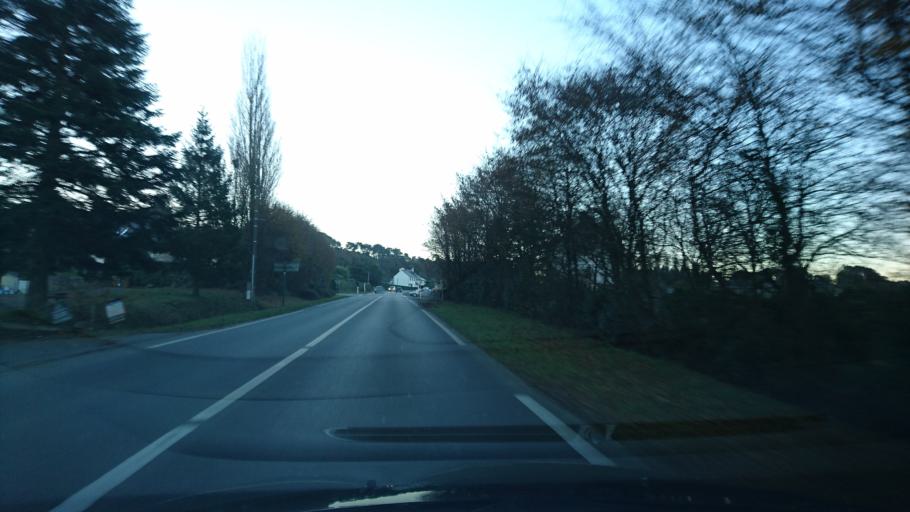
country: FR
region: Brittany
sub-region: Departement des Cotes-d'Armor
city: Pledran
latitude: 48.4576
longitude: -2.7550
